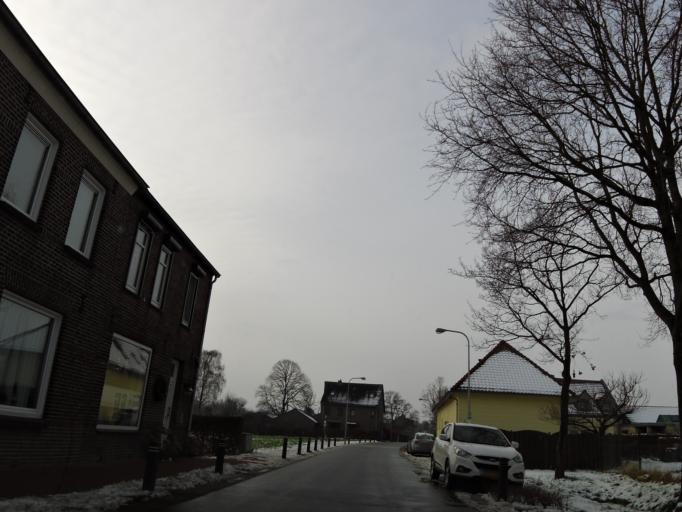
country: NL
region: Limburg
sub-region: Gemeente Voerendaal
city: Voerendaal
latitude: 50.8941
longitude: 5.9191
